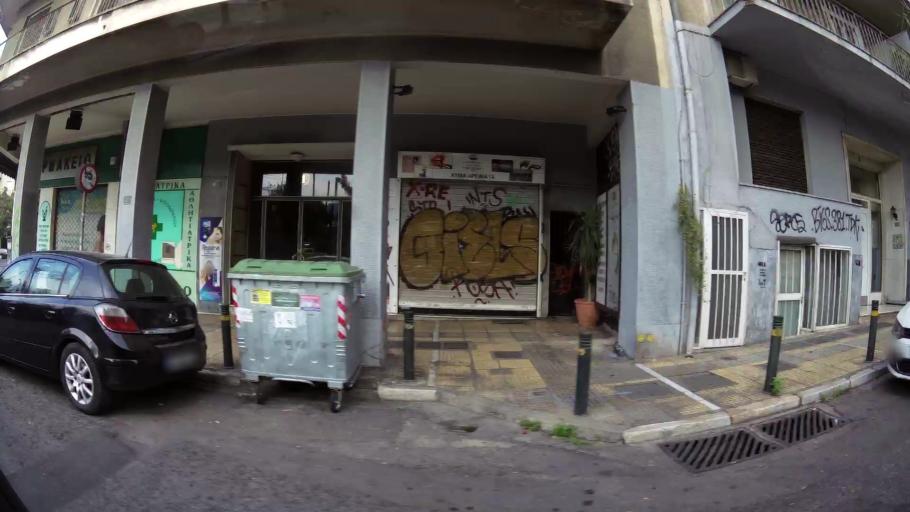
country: GR
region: Attica
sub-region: Nomarchia Athinas
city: Kipseli
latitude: 37.9955
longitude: 23.7340
